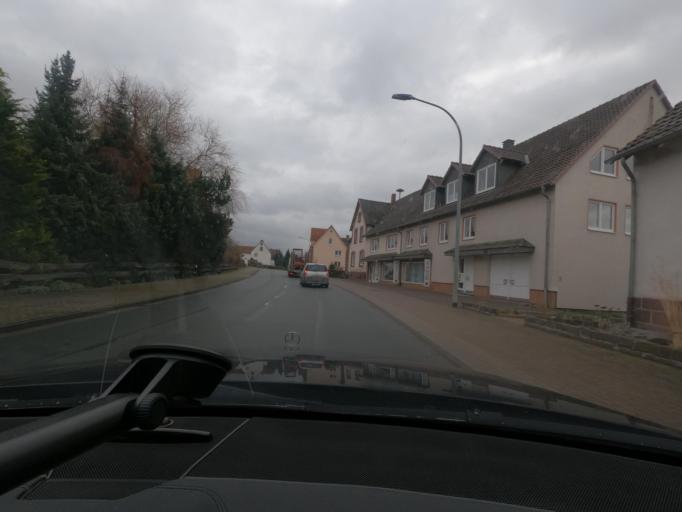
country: DE
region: Hesse
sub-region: Regierungsbezirk Kassel
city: Volkmarsen
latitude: 51.3856
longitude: 9.1443
